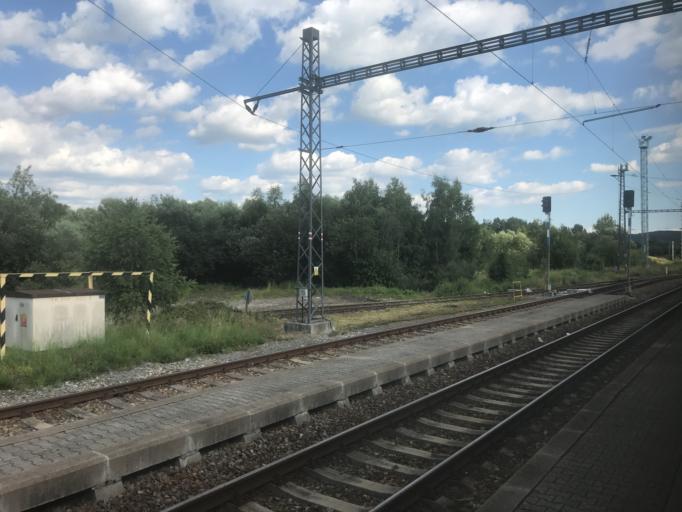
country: CZ
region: Jihocesky
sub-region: Okres Cesky Krumlov
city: Dolni Dvoriste
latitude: 48.6482
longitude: 14.4322
